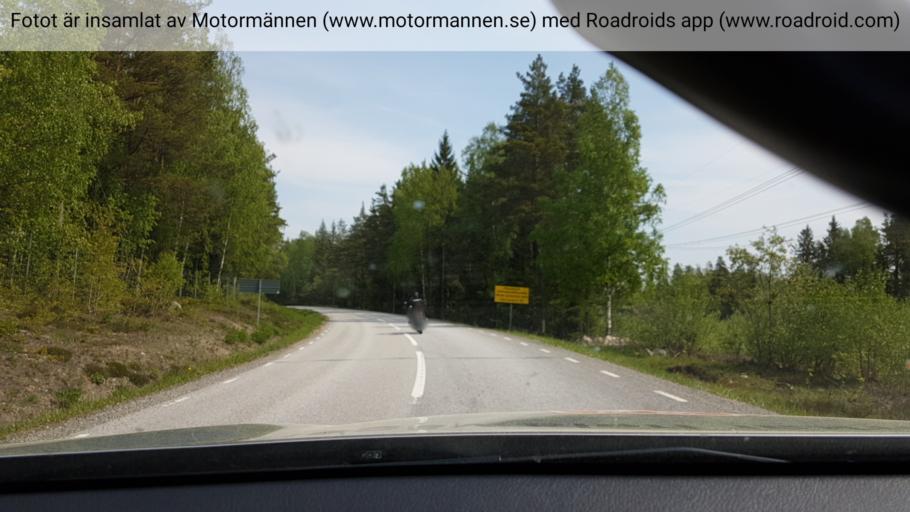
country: SE
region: Stockholm
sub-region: Botkyrka Kommun
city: Tullinge
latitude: 59.1228
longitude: 17.9006
